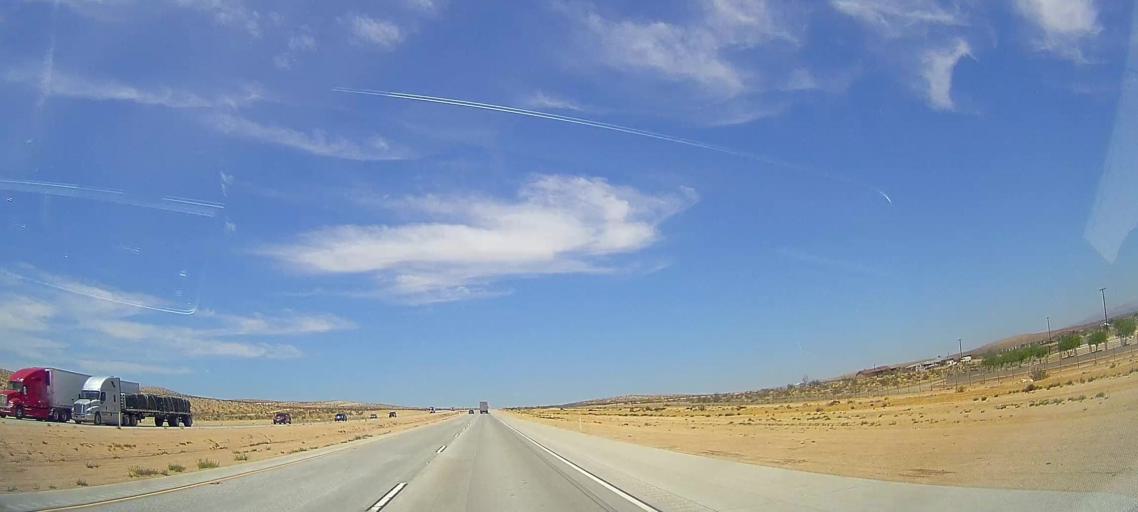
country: US
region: California
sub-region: San Bernardino County
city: Lenwood
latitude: 34.9139
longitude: -117.2206
